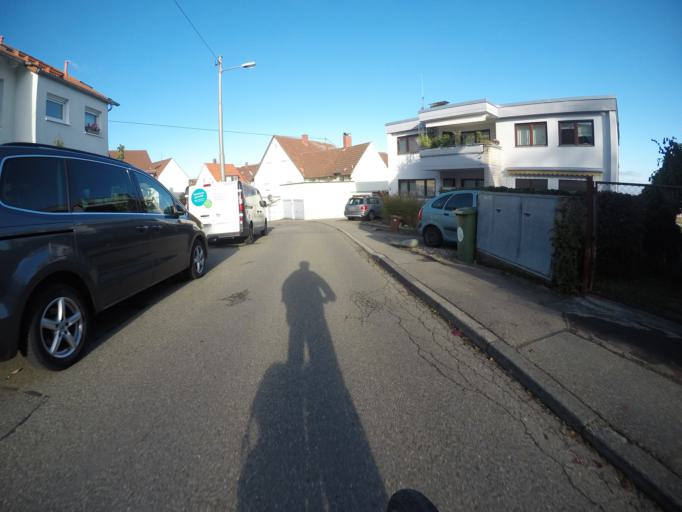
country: DE
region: Baden-Wuerttemberg
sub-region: Regierungsbezirk Stuttgart
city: Steinenbronn
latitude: 48.7172
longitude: 9.1002
